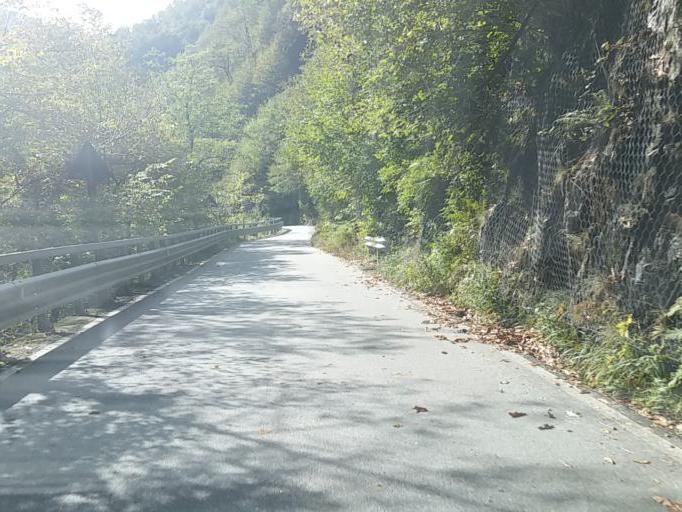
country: IT
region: Piedmont
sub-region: Provincia Verbano-Cusio-Ossola
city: Falmenta
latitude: 46.0828
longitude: 8.6008
